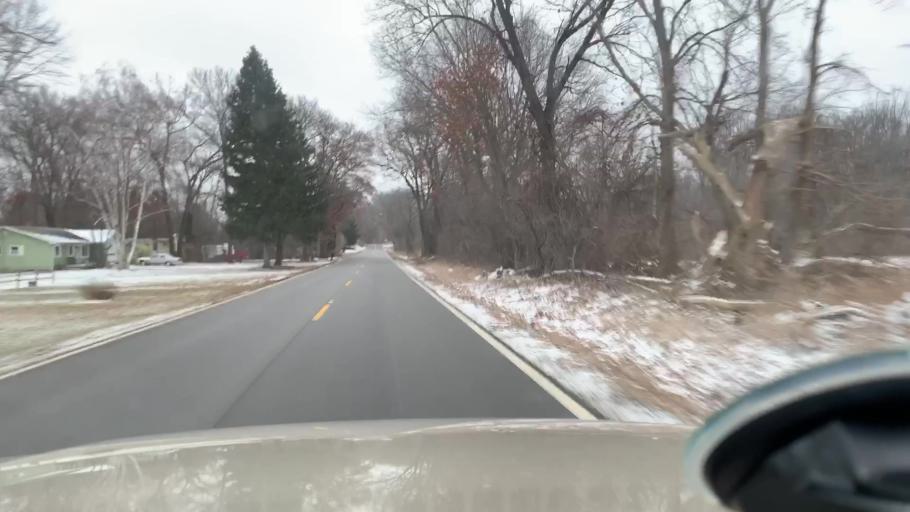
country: US
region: Michigan
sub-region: Jackson County
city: Spring Arbor
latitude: 42.2047
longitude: -84.5309
